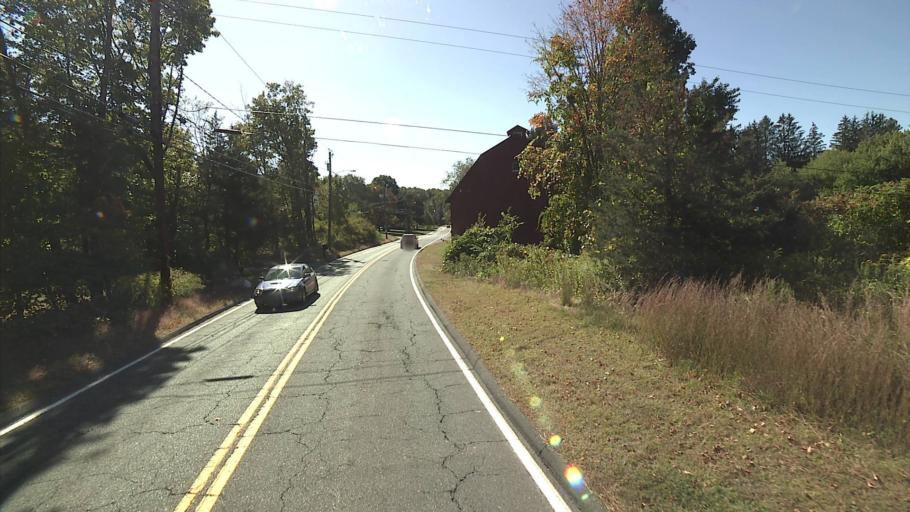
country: US
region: Connecticut
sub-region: Hartford County
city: Bristol
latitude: 41.7141
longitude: -72.9462
